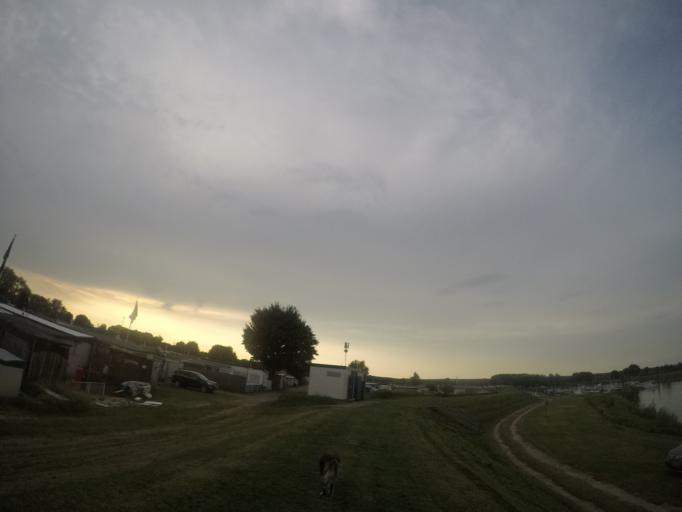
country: NL
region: Gelderland
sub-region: Gemeente Rheden
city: Rheden
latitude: 51.9940
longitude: 6.0383
